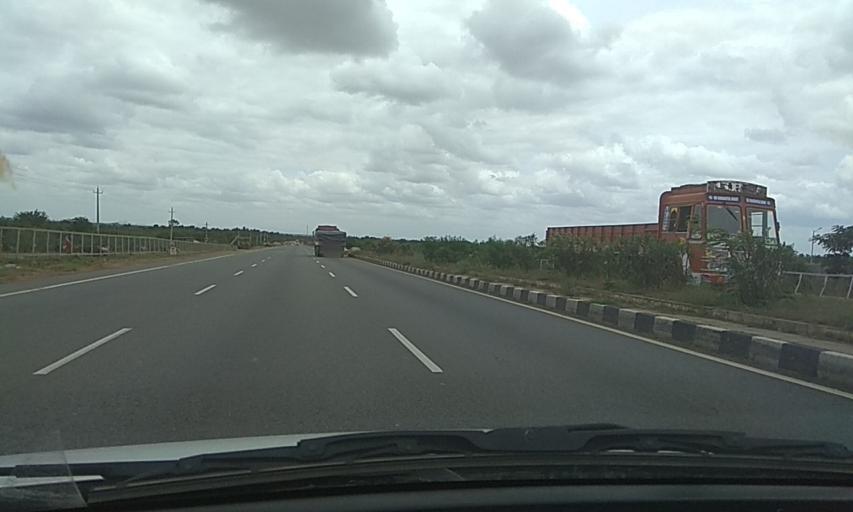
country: IN
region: Karnataka
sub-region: Tumkur
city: Sira
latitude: 13.8295
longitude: 76.7643
